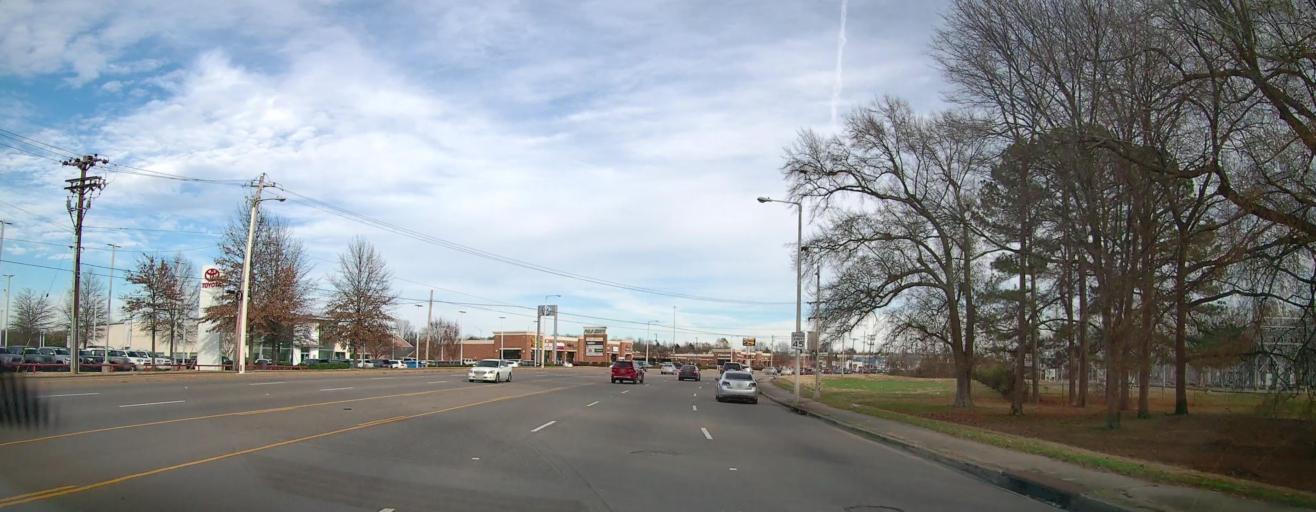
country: US
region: Tennessee
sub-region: Shelby County
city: Germantown
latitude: 35.0501
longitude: -89.8174
